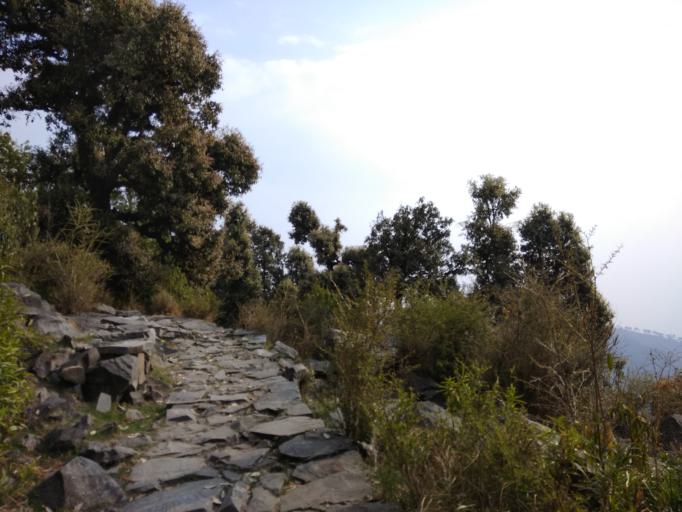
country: IN
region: Himachal Pradesh
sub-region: Kangra
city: Dharmsala
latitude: 32.2705
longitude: 76.3146
